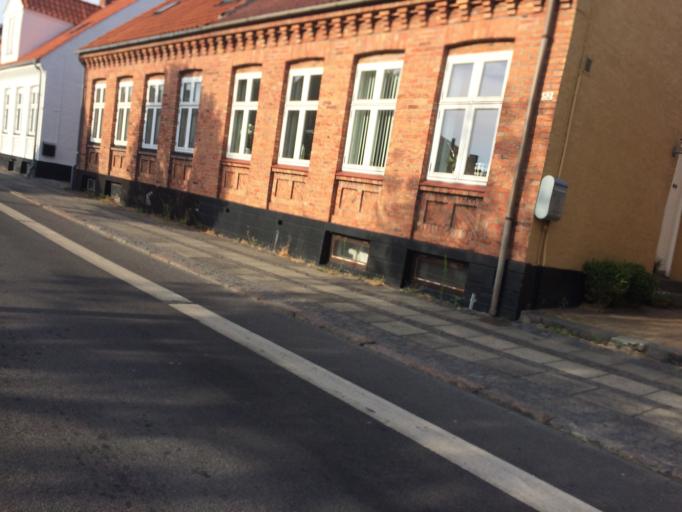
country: DK
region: Capital Region
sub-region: Bornholm Kommune
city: Ronne
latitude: 55.1061
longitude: 14.7027
